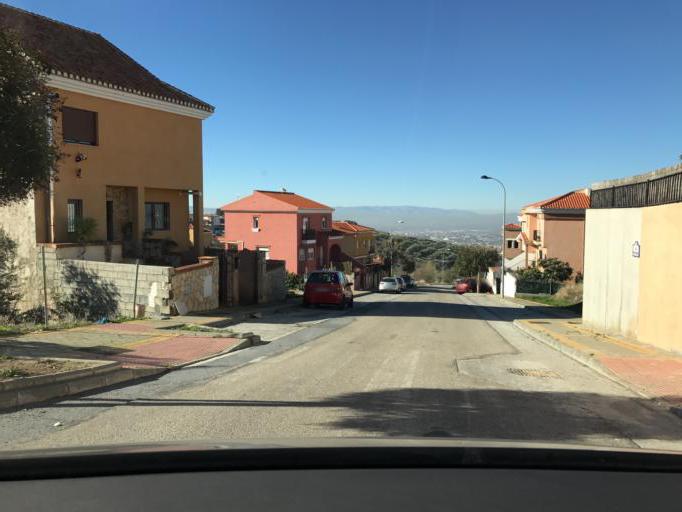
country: ES
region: Andalusia
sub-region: Provincia de Granada
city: Alfacar
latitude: 37.2187
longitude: -3.5743
